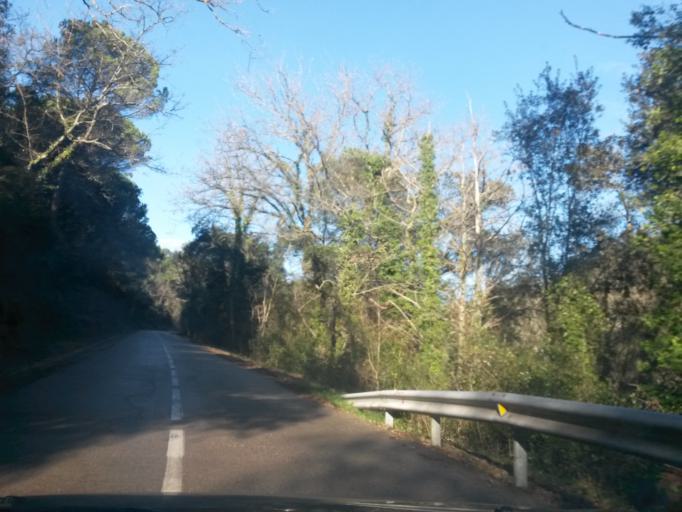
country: ES
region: Catalonia
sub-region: Provincia de Girona
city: Angles
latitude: 41.9967
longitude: 2.6705
